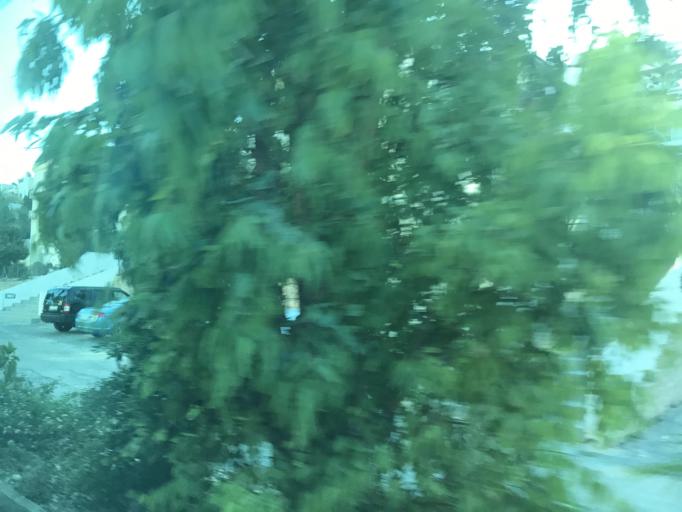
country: ES
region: Valencia
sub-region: Provincia de Alicante
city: Torrevieja
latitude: 38.0030
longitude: -0.6505
